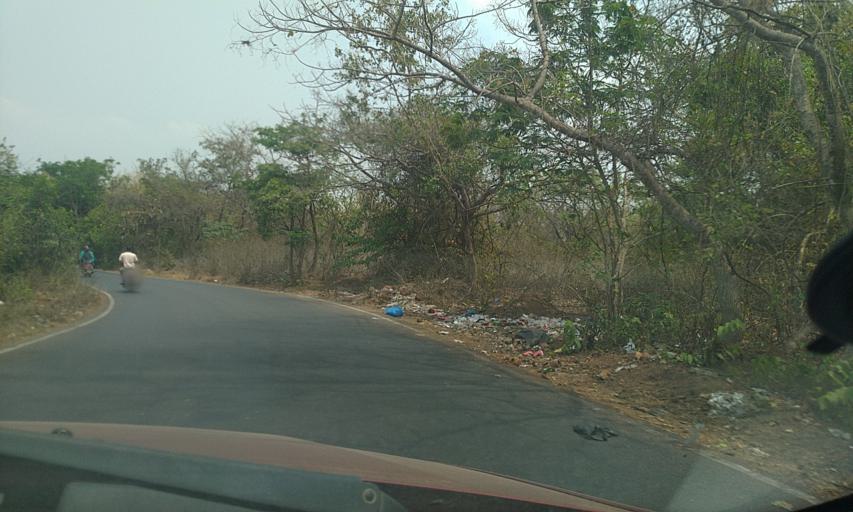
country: IN
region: Goa
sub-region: North Goa
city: Mapuca
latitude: 15.6112
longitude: 73.7956
